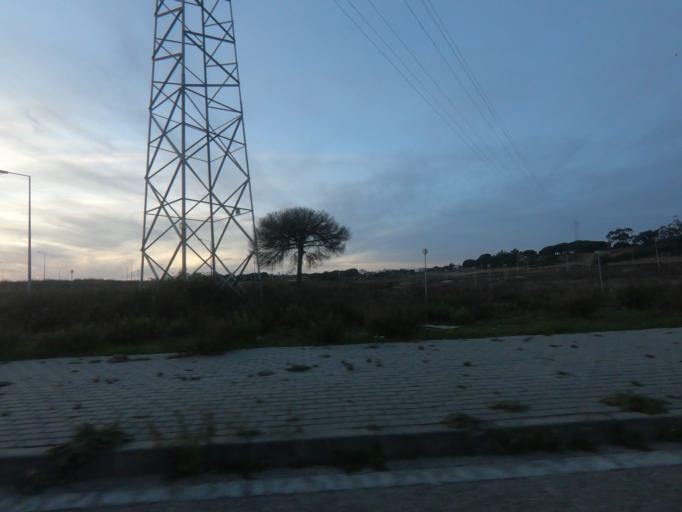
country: PT
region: Setubal
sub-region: Setubal
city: Setubal
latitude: 38.5153
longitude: -8.8521
